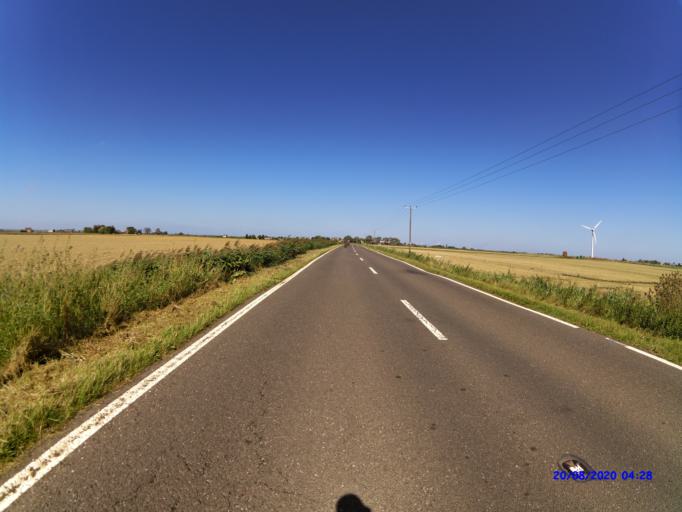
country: GB
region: England
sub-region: Cambridgeshire
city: Whittlesey
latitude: 52.5045
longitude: -0.1346
